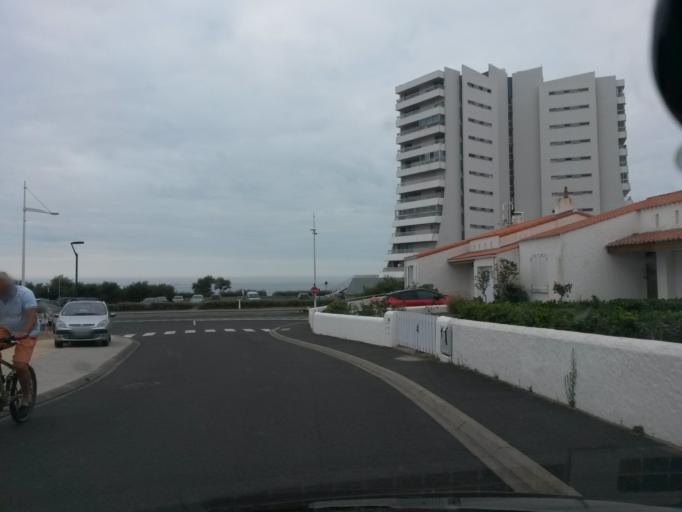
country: FR
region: Pays de la Loire
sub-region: Departement de la Vendee
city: Les Sables-d'Olonne
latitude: 46.4900
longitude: -1.7992
